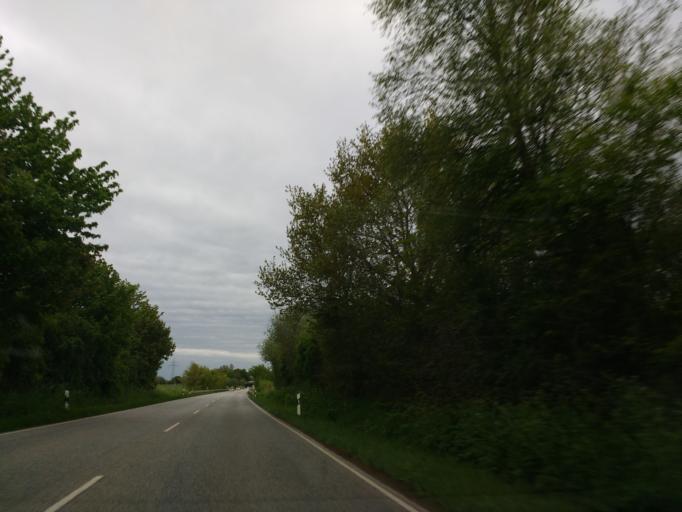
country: DE
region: Schleswig-Holstein
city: Brodersby
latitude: 54.6433
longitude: 9.9601
